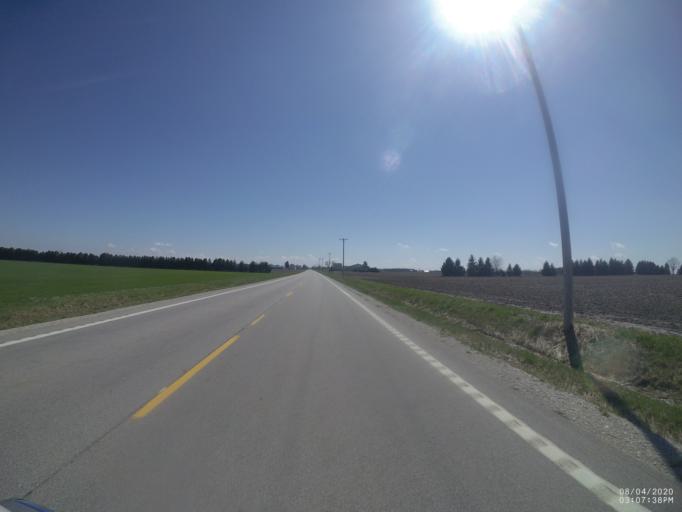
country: US
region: Ohio
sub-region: Sandusky County
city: Stony Prairie
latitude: 41.2945
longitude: -83.2357
